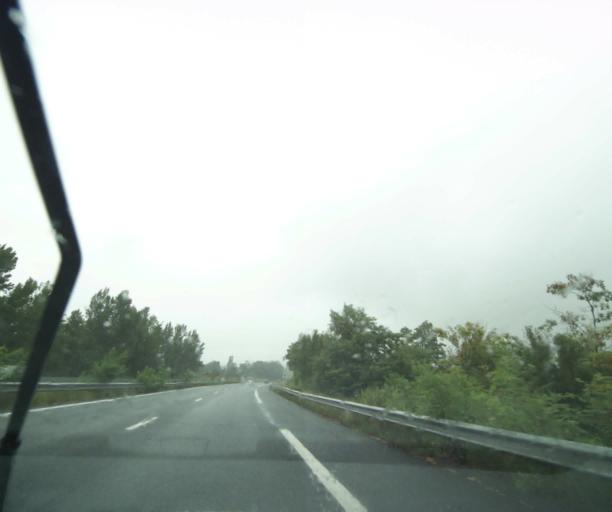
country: FR
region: Midi-Pyrenees
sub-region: Departement du Tarn
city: Montans
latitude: 43.8715
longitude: 1.8991
